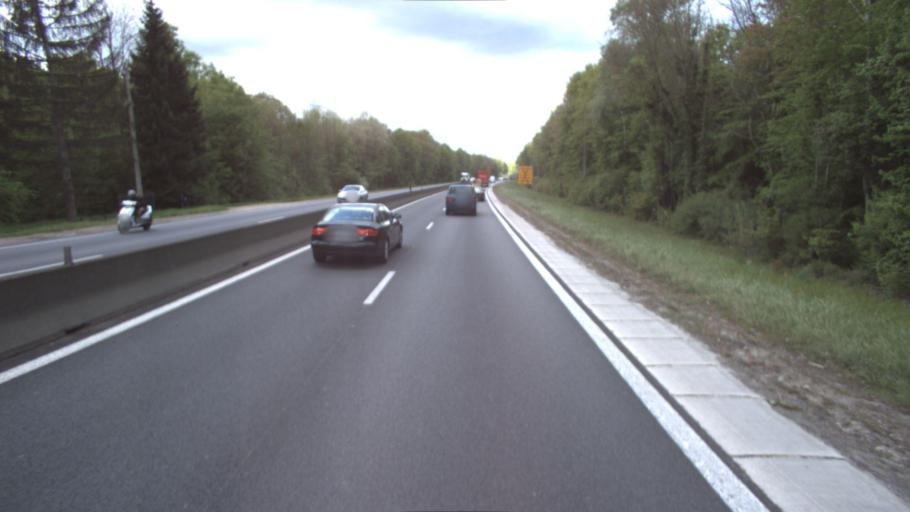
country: FR
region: Ile-de-France
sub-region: Departement de Seine-et-Marne
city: Gretz-Armainvilliers
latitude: 48.7337
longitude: 2.7126
